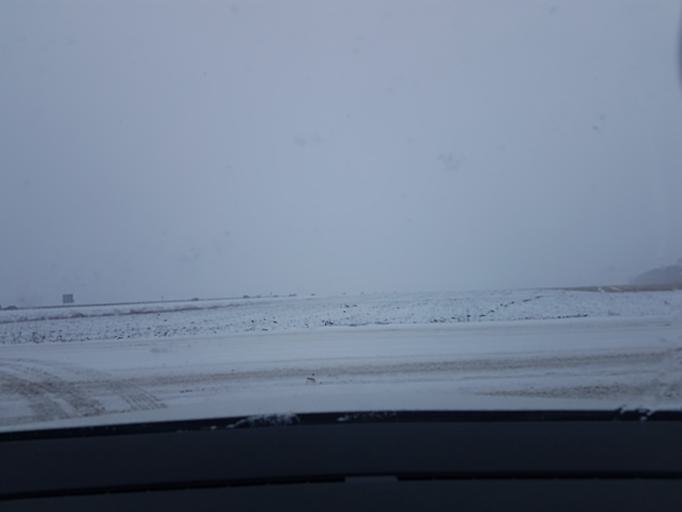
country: RU
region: Rjazan
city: Ryazhsk
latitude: 53.6573
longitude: 39.9825
